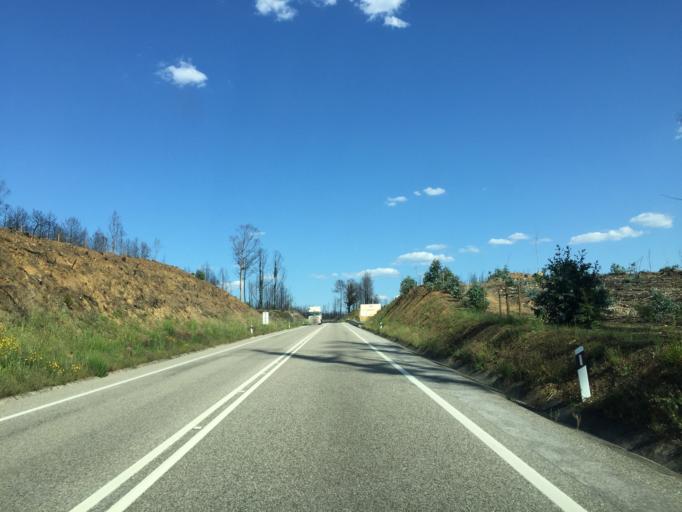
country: PT
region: Leiria
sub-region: Pedrogao Grande
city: Pedrogao Grande
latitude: 39.9269
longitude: -8.1781
